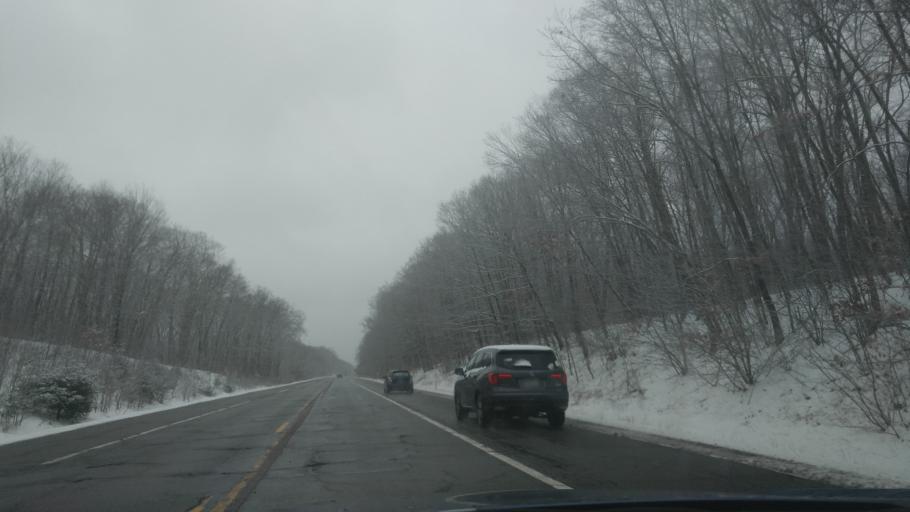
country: US
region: Rhode Island
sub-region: Providence County
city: North Scituate
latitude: 41.8380
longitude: -71.6244
